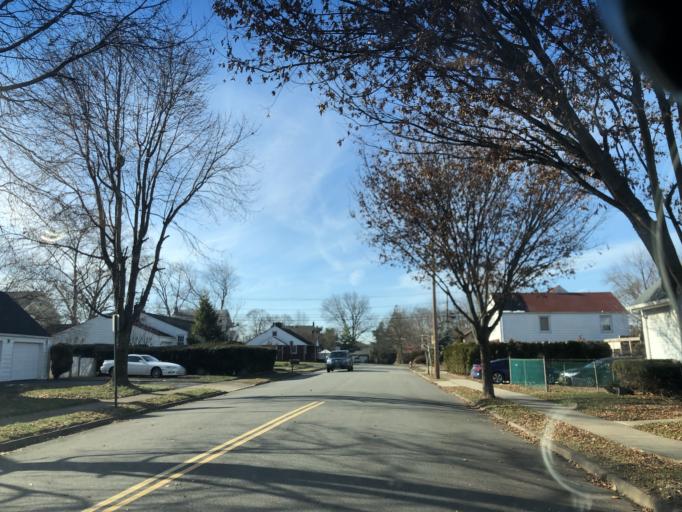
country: US
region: New Jersey
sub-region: Bergen County
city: Elmwood Park
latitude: 40.9222
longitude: -74.1209
